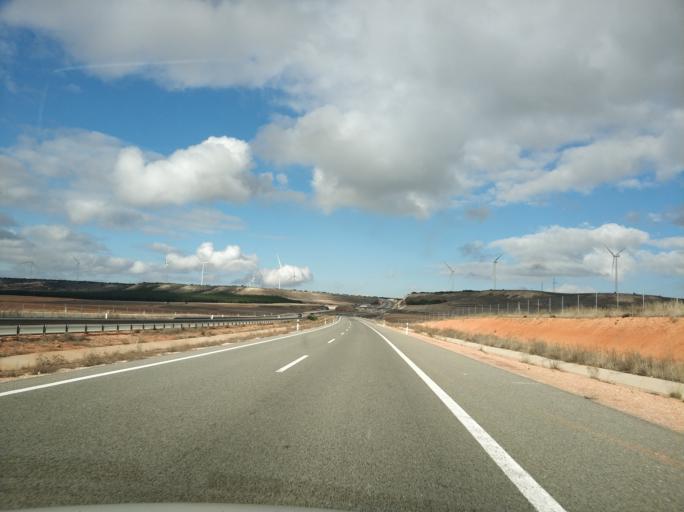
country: ES
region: Castille and Leon
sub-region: Provincia de Soria
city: Alcubilla de las Penas
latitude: 41.2771
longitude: -2.4747
